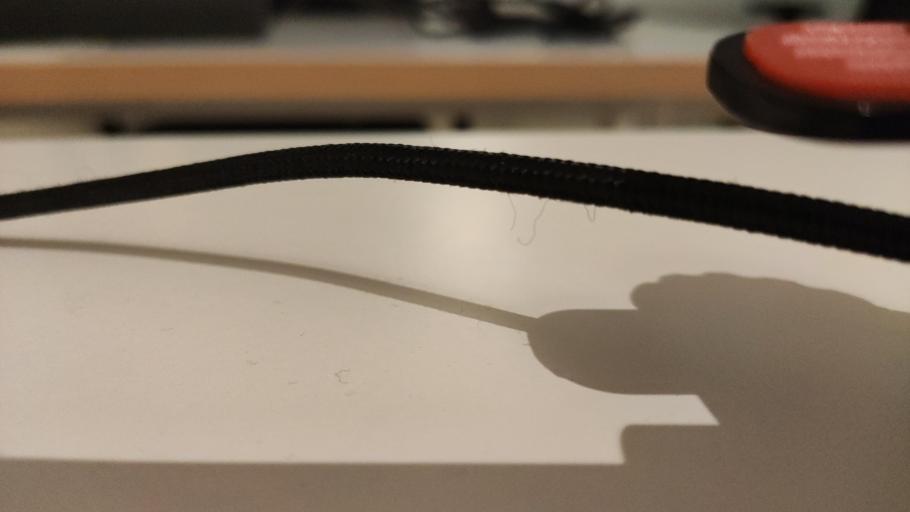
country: RU
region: Moskovskaya
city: Il'inskiy Pogost
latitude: 55.5276
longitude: 38.8722
